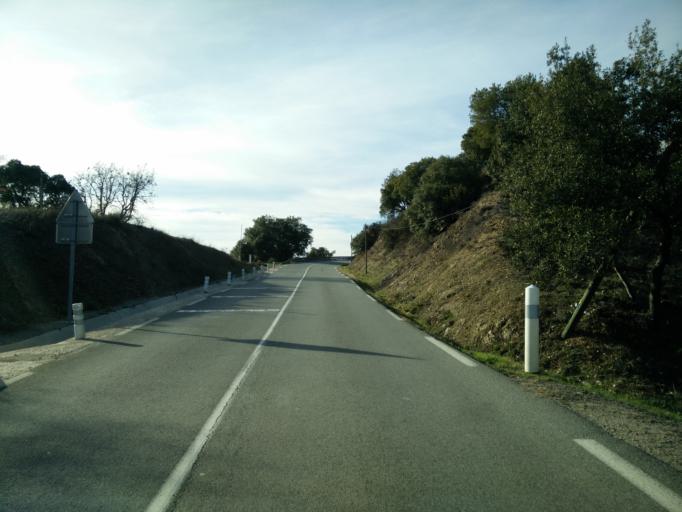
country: FR
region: Provence-Alpes-Cote d'Azur
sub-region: Departement du Var
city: Montauroux
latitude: 43.5851
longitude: 6.7984
